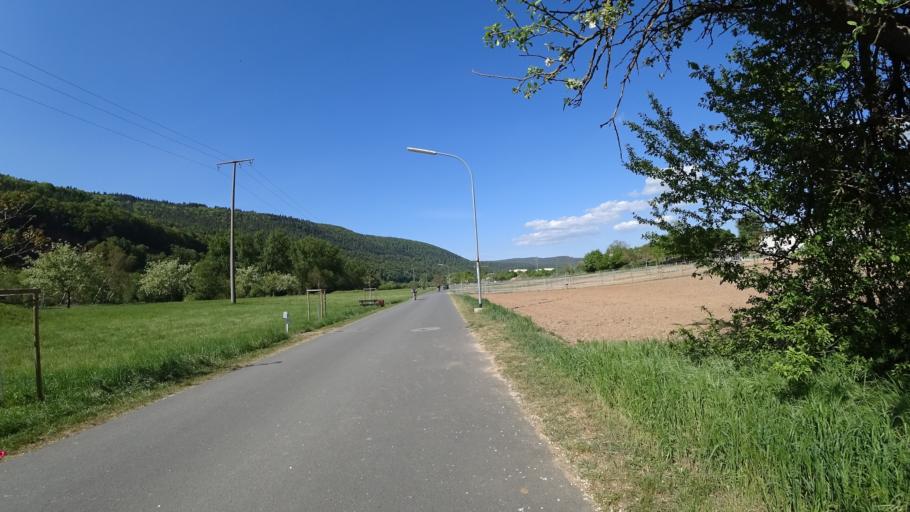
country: DE
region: Bavaria
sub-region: Regierungsbezirk Unterfranken
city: Burgstadt
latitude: 49.7228
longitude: 9.2678
